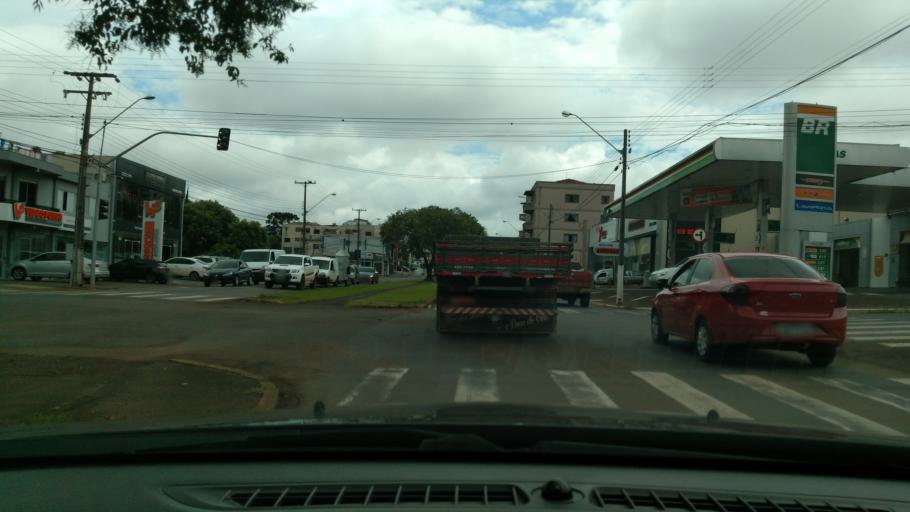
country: BR
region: Parana
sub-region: Guarapuava
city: Guarapuava
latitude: -25.3848
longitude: -51.4713
